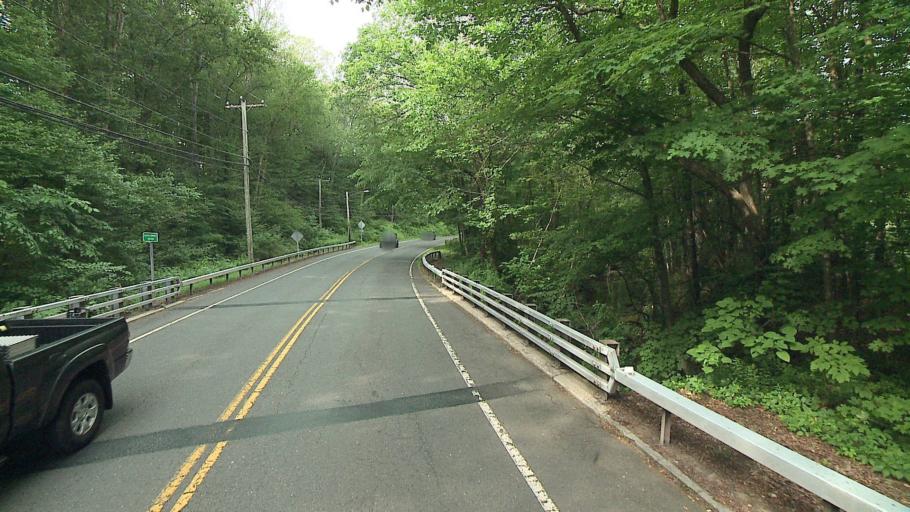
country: US
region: Connecticut
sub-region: Hartford County
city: Collinsville
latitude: 41.8203
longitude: -72.9141
